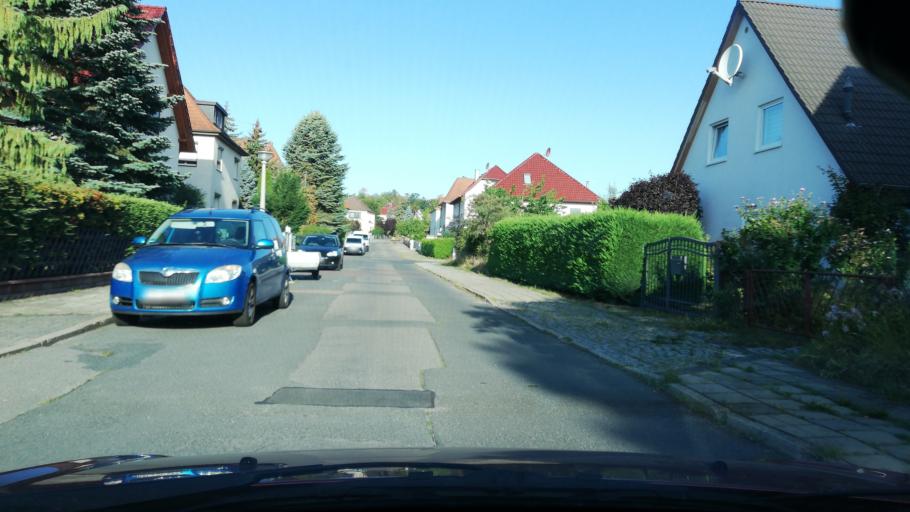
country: DE
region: Saxony-Anhalt
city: Halle Neustadt
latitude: 51.4912
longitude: 11.9098
